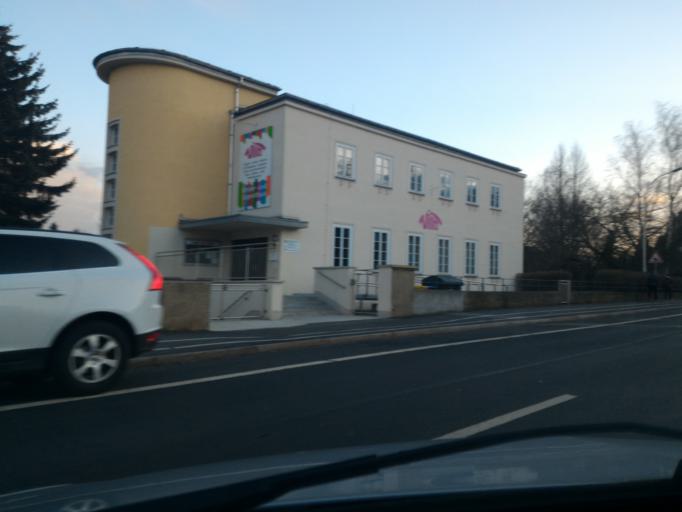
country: DE
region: Saxony
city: Zittau
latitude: 50.8897
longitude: 14.8045
